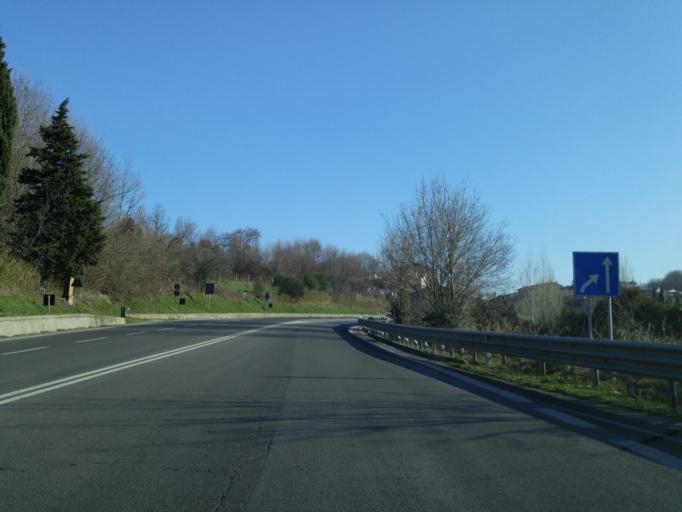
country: IT
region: The Marches
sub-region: Provincia di Pesaro e Urbino
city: Gradara
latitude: 43.9448
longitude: 12.8199
